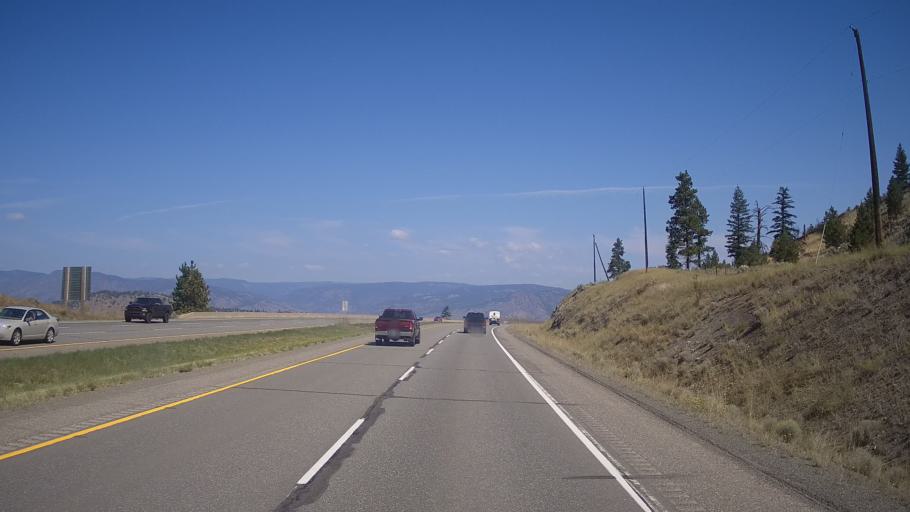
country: CA
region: British Columbia
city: Kamloops
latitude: 50.6465
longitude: -120.4863
